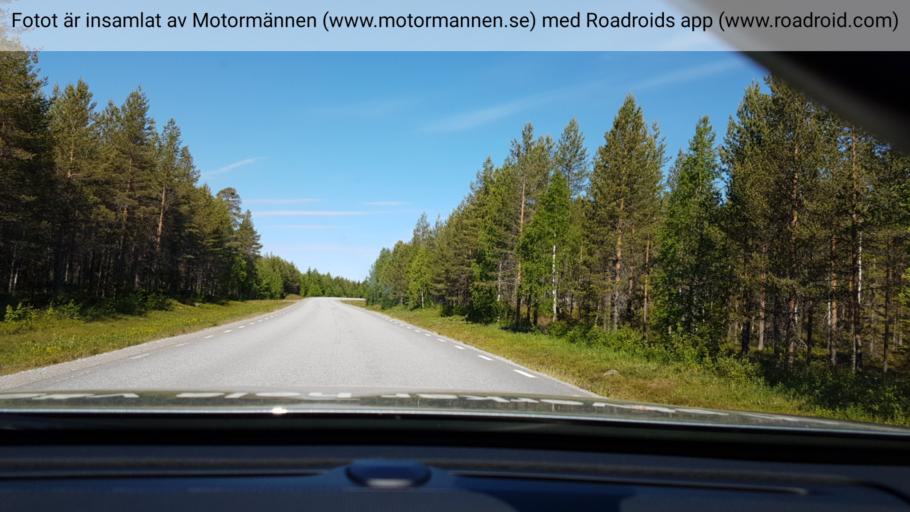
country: SE
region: Vaesterbotten
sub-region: Bjurholms Kommun
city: Bjurholm
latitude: 64.0162
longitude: 18.6888
